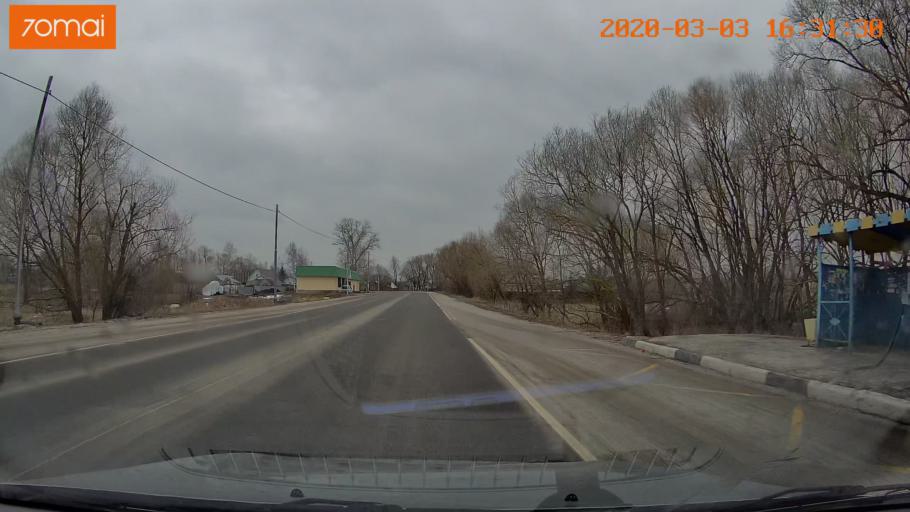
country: RU
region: Moskovskaya
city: Konobeyevo
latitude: 55.4248
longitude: 38.7254
